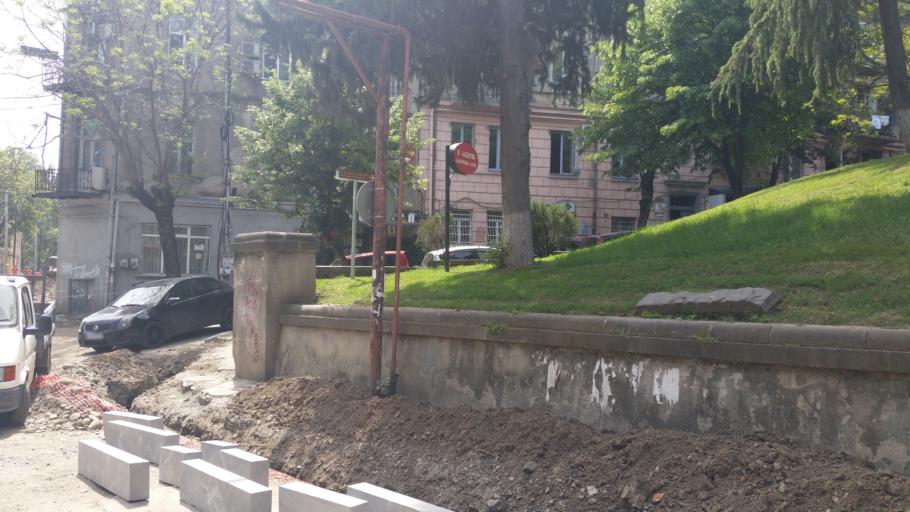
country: GE
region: T'bilisi
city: Tbilisi
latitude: 41.6981
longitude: 44.8009
